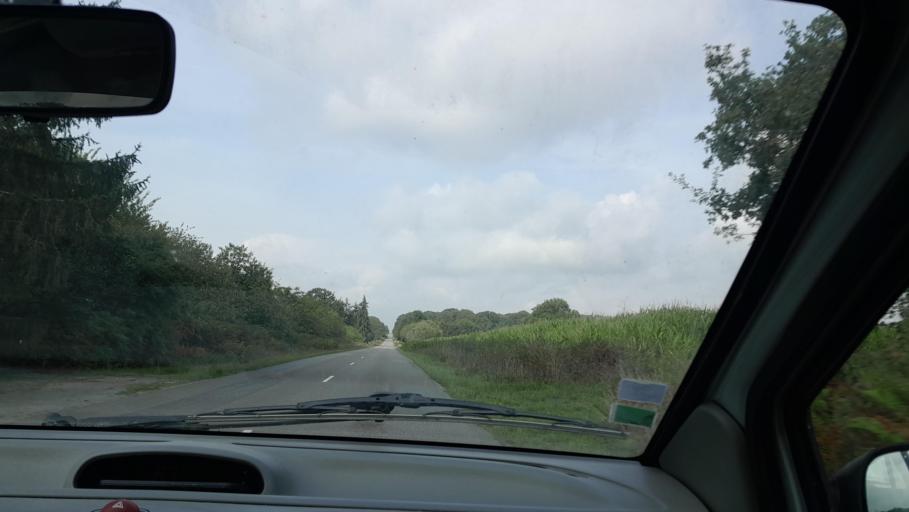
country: FR
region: Pays de la Loire
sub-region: Departement de la Mayenne
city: Ballots
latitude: 47.9619
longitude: -1.0020
